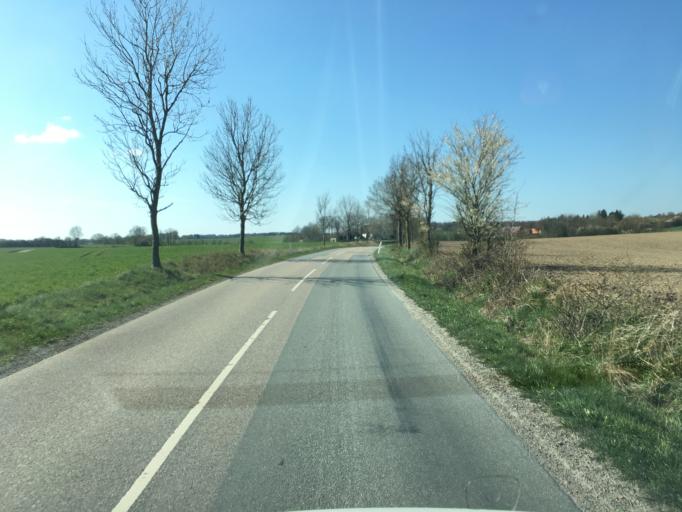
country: DK
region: South Denmark
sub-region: Sonderborg Kommune
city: Grasten
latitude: 54.9038
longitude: 9.5518
